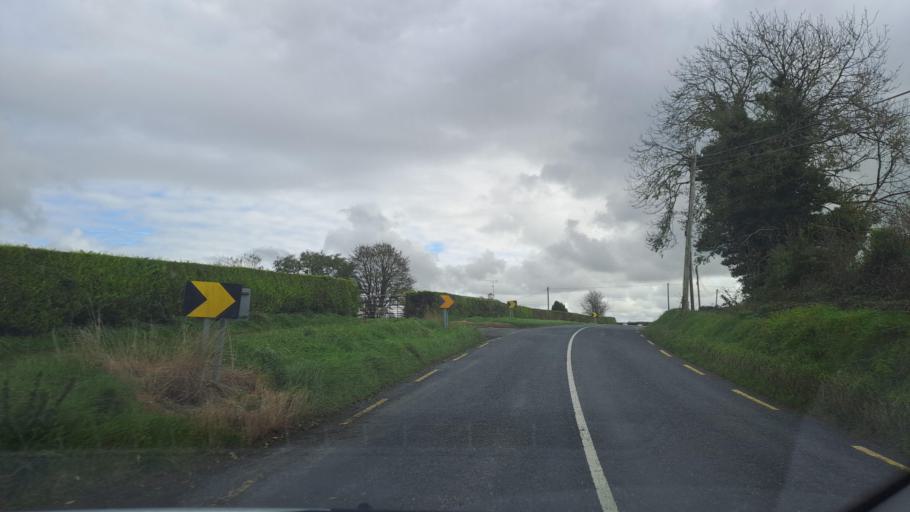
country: IE
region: Ulster
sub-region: An Cabhan
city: Virginia
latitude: 53.8329
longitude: -7.0385
